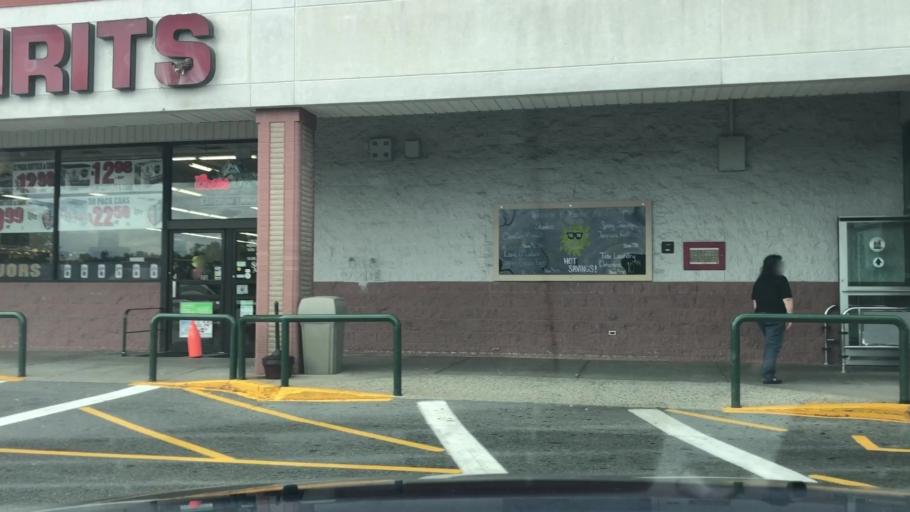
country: US
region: Massachusetts
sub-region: Middlesex County
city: Tewksbury
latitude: 42.6312
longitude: -71.2722
